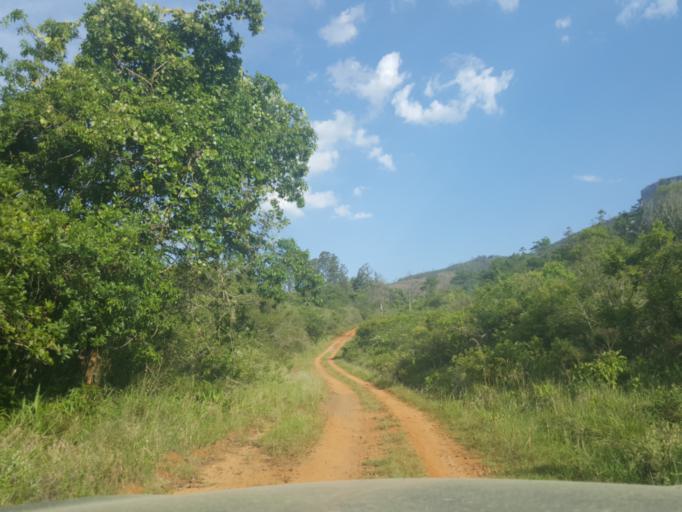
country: ZA
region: Limpopo
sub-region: Mopani District Municipality
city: Hoedspruit
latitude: -24.5953
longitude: 30.8484
